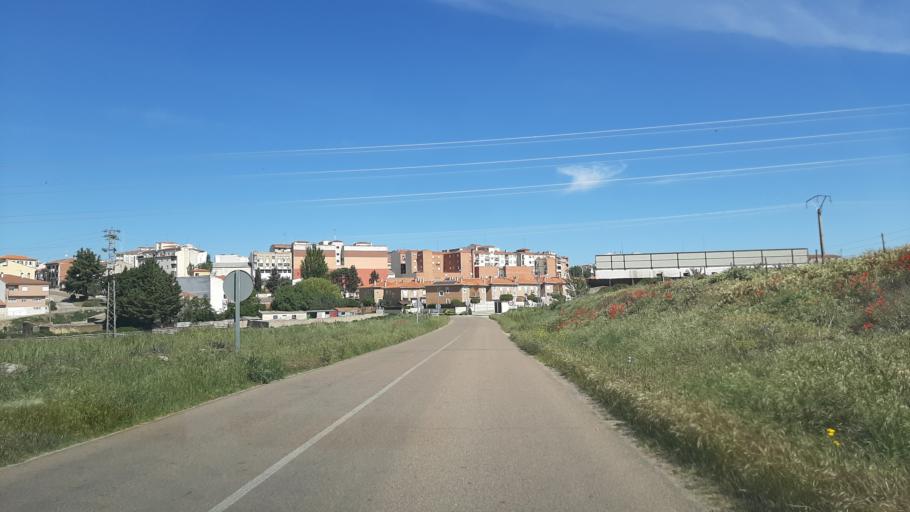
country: ES
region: Castille and Leon
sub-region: Provincia de Salamanca
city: Alba de Tormes
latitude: 40.8227
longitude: -5.5067
